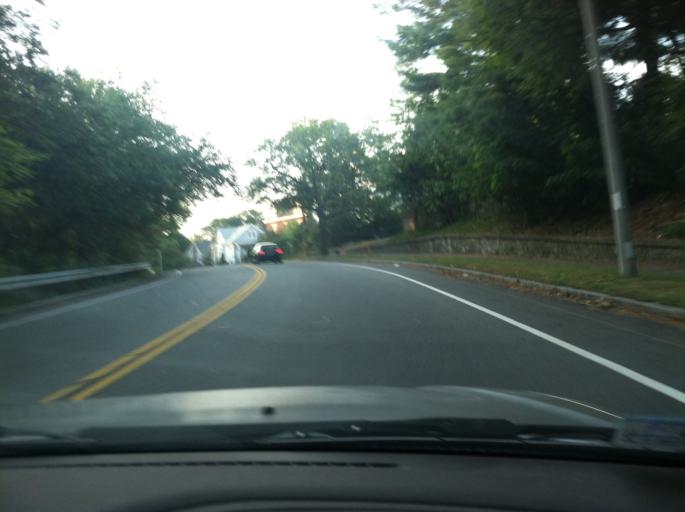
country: US
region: Massachusetts
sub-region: Middlesex County
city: Arlington
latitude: 42.4218
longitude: -71.1468
